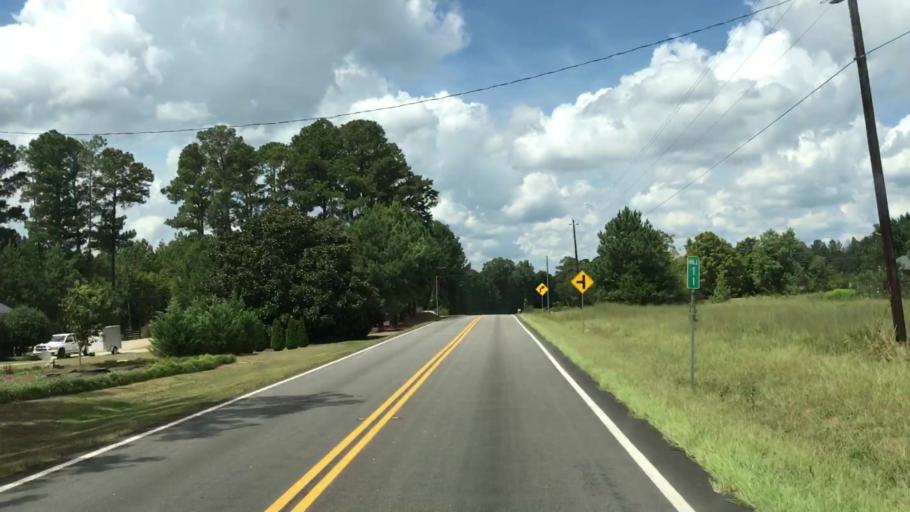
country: US
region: Georgia
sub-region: Greene County
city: Greensboro
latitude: 33.5592
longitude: -83.1337
